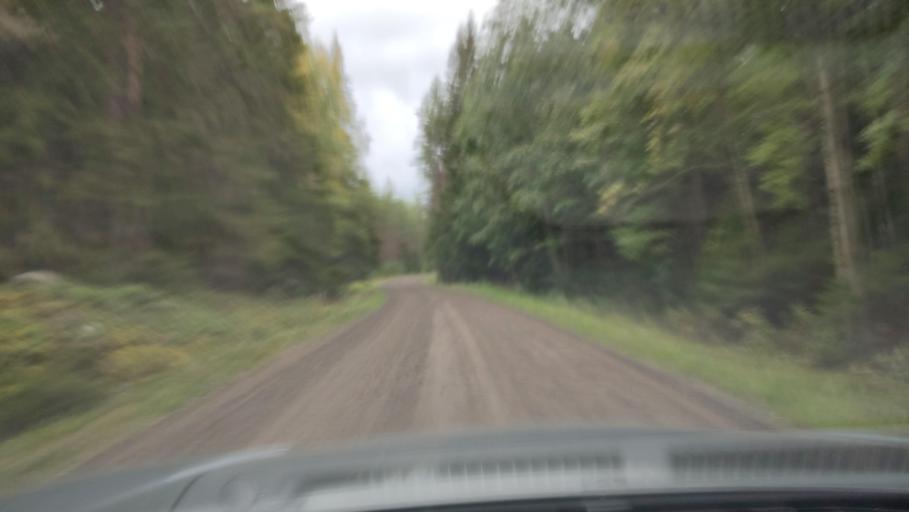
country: FI
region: Southern Ostrobothnia
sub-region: Suupohja
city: Karijoki
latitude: 62.2287
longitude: 21.5727
